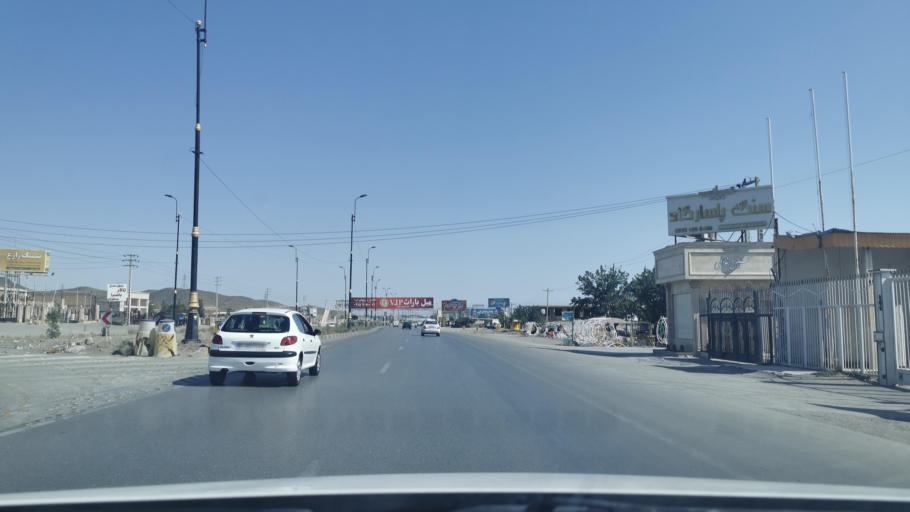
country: IR
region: Razavi Khorasan
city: Torqabeh
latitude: 36.3730
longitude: 59.4175
